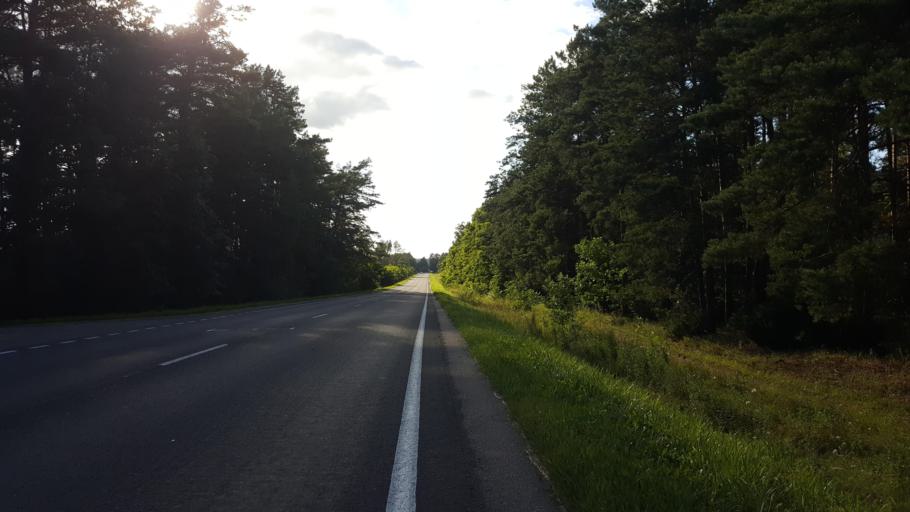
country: BY
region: Brest
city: Kamyanyets
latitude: 52.3982
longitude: 23.9096
